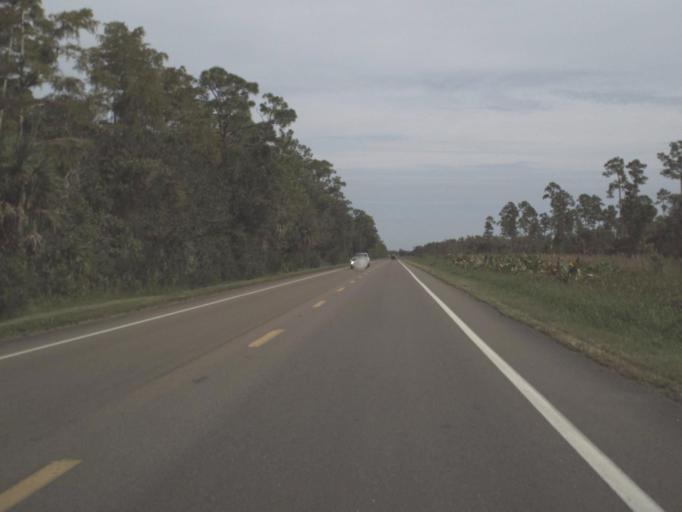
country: US
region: Florida
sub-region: Lee County
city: Olga
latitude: 26.9292
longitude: -81.7606
